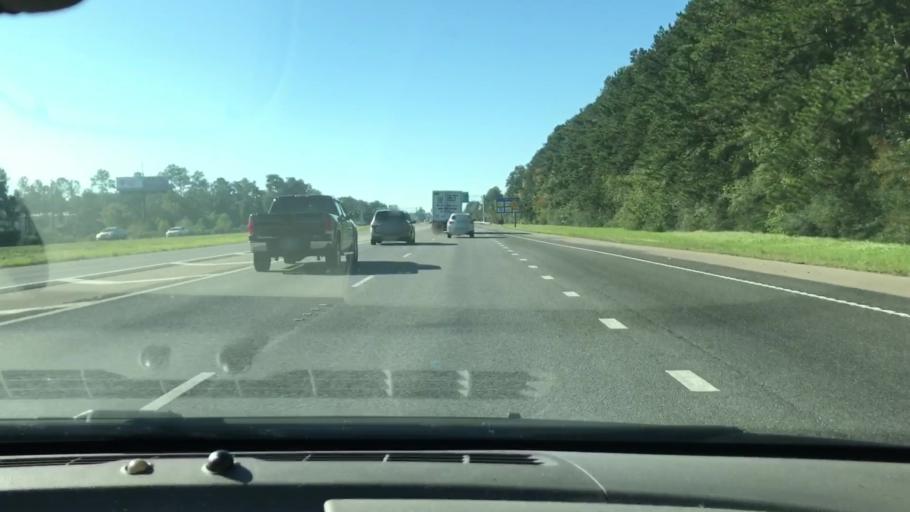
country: US
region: Louisiana
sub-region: Saint Tammany Parish
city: Slidell
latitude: 30.3001
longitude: -89.7441
